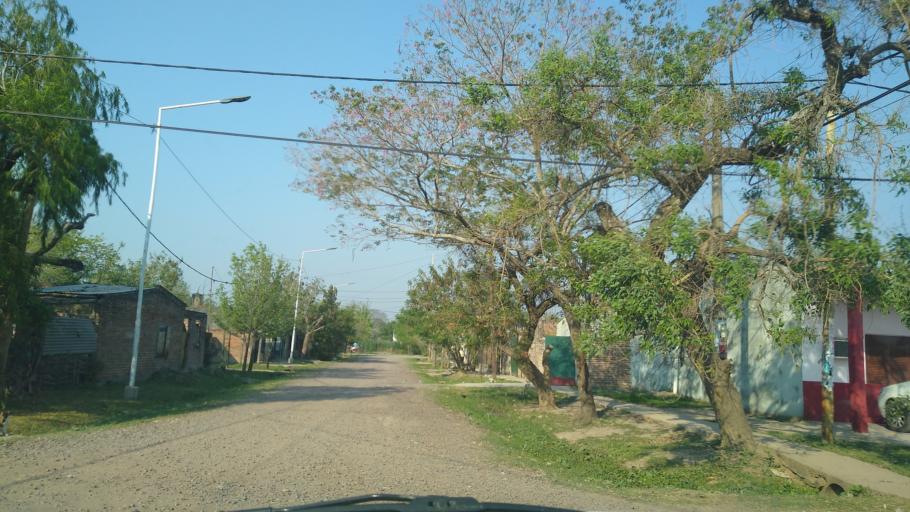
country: AR
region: Chaco
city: Barranqueras
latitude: -27.4761
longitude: -58.9501
